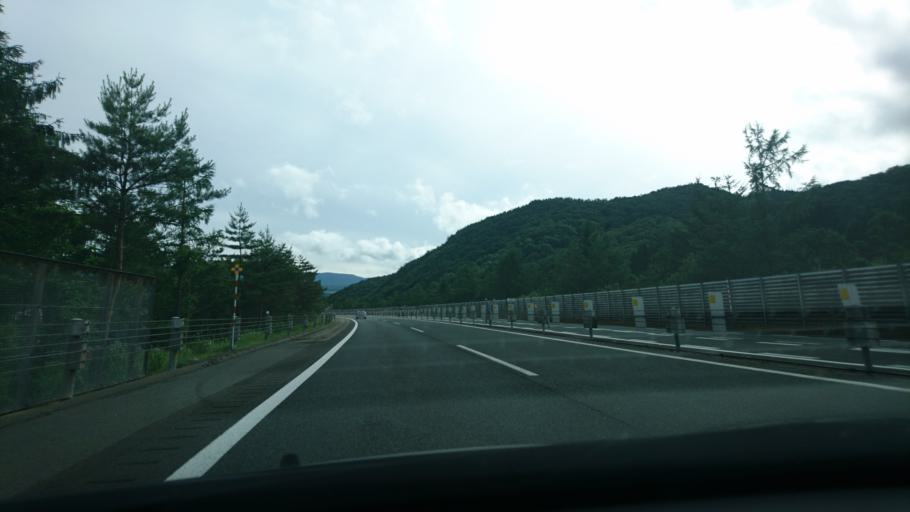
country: JP
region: Akita
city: Hanawa
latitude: 40.0439
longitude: 140.9949
